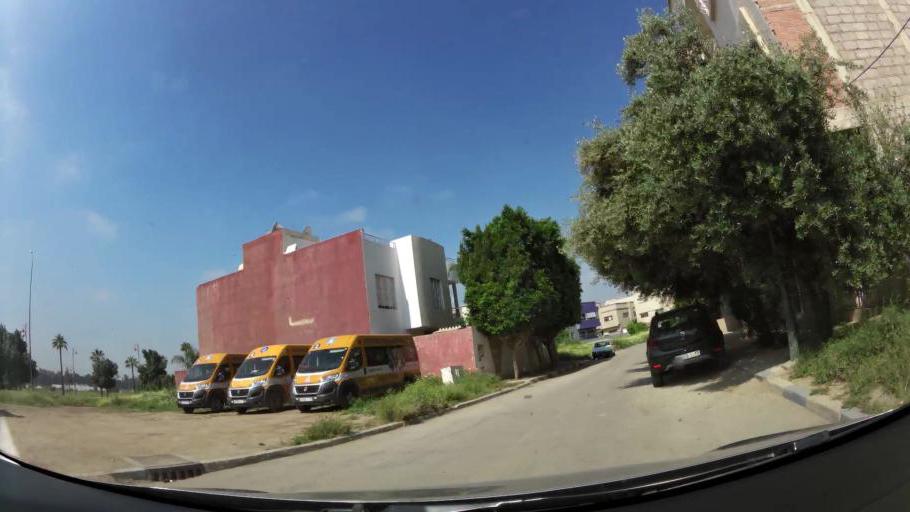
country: MA
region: Fes-Boulemane
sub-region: Fes
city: Fes
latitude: 34.0545
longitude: -5.0245
